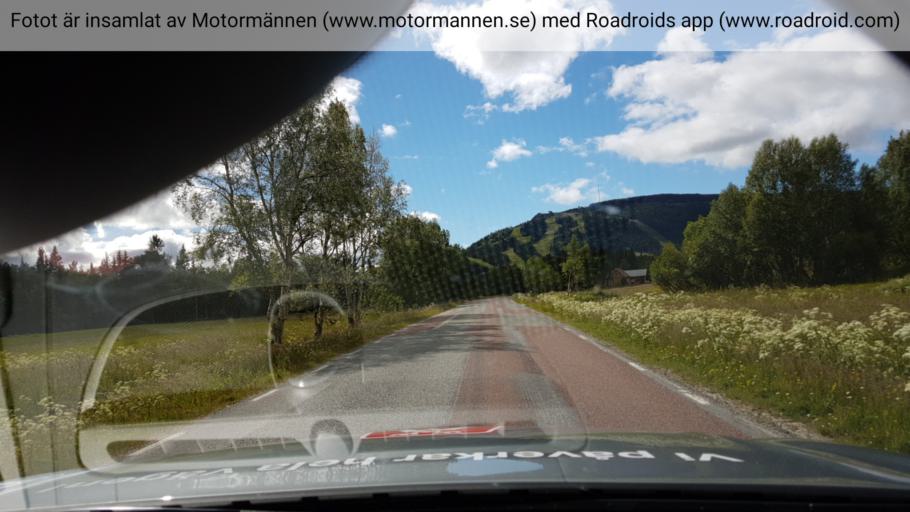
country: SE
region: Jaemtland
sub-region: Are Kommun
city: Are
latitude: 62.5494
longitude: 12.6017
